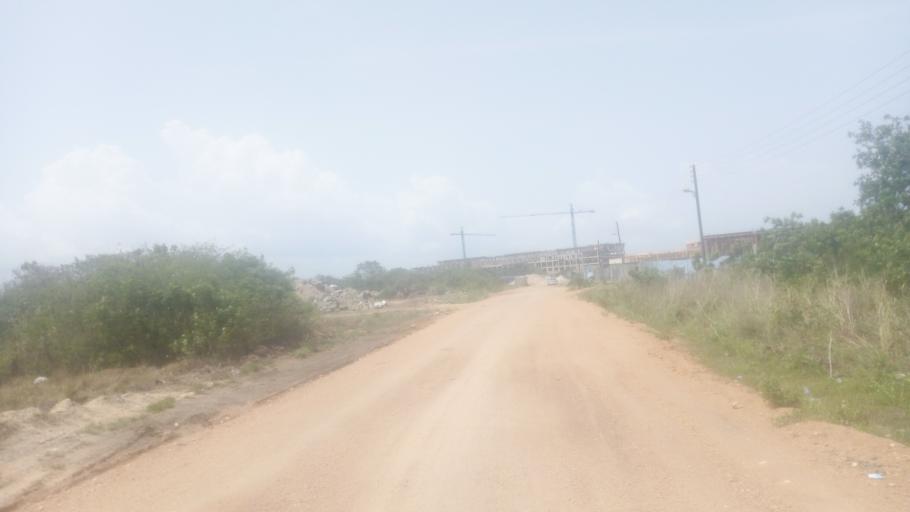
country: GH
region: Central
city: Winneba
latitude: 5.3679
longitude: -0.6331
